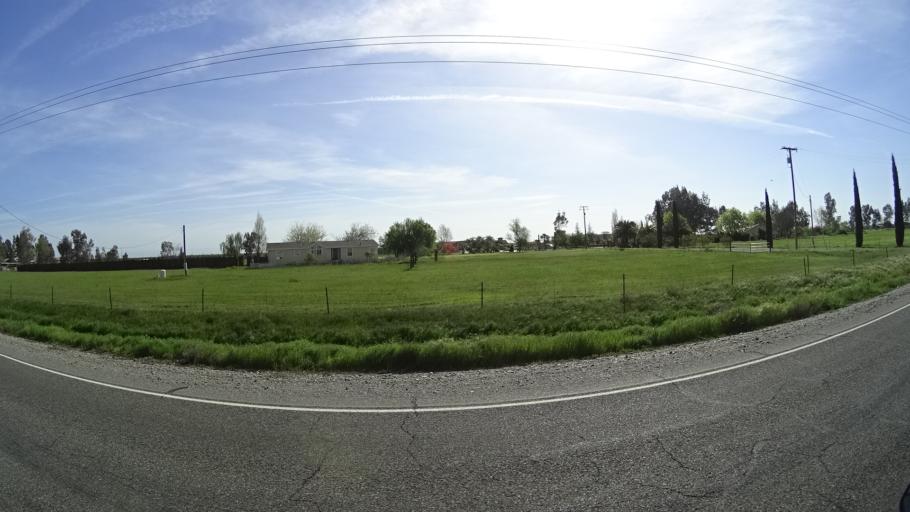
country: US
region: California
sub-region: Glenn County
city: Orland
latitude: 39.6408
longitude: -122.1974
